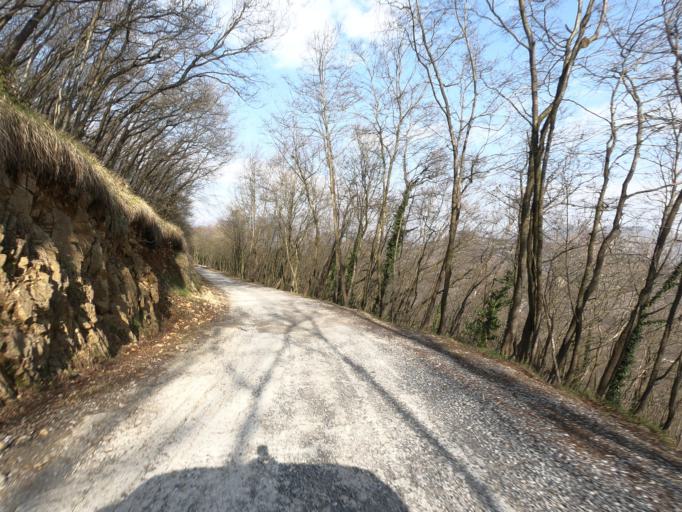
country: IT
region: Liguria
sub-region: Provincia di Savona
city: Balestrino
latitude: 44.1120
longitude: 8.1567
